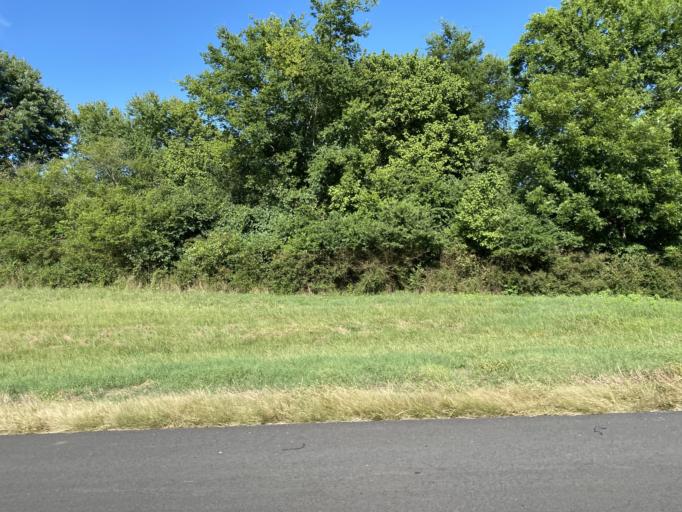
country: US
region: Alabama
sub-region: Limestone County
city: Athens
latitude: 34.7637
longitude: -86.9388
